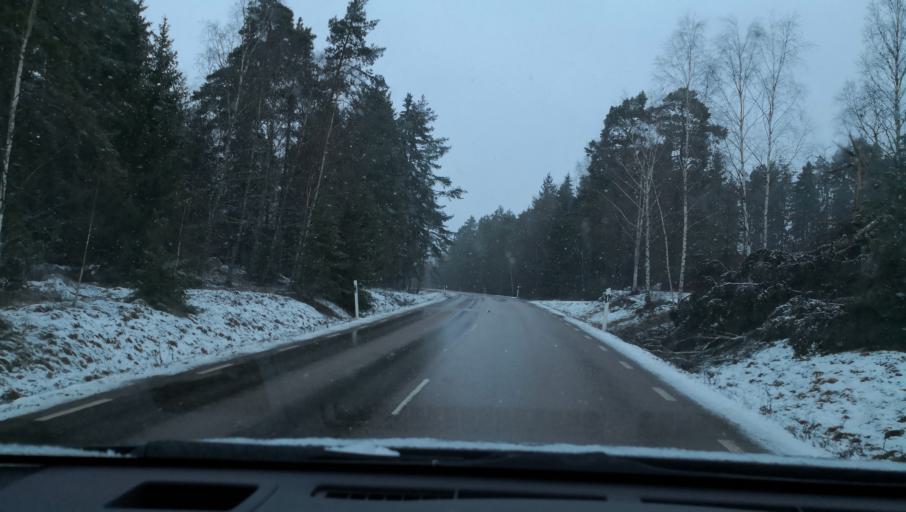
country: SE
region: Vaestmanland
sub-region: Hallstahammars Kommun
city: Kolback
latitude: 59.5873
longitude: 16.3562
